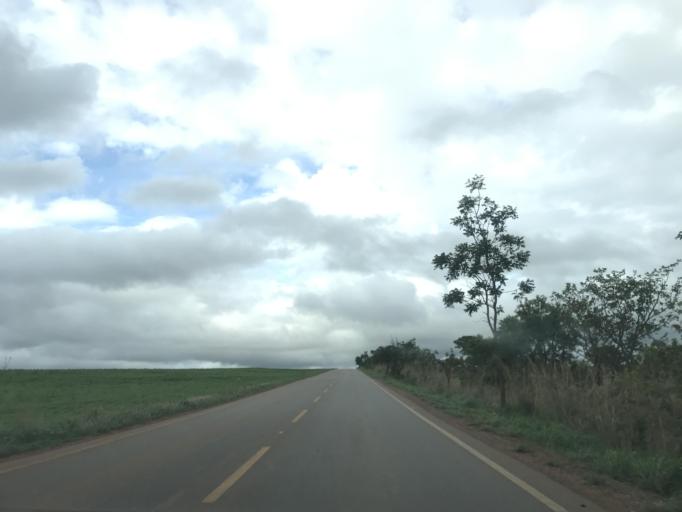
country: BR
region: Goias
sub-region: Vianopolis
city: Vianopolis
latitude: -16.5606
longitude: -48.2834
